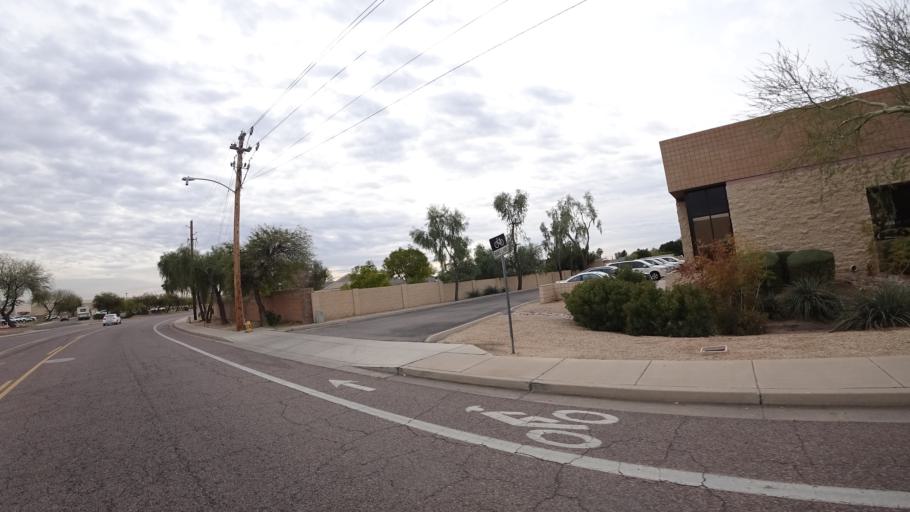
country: US
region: Arizona
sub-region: Maricopa County
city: Glendale
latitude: 33.6468
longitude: -112.1171
